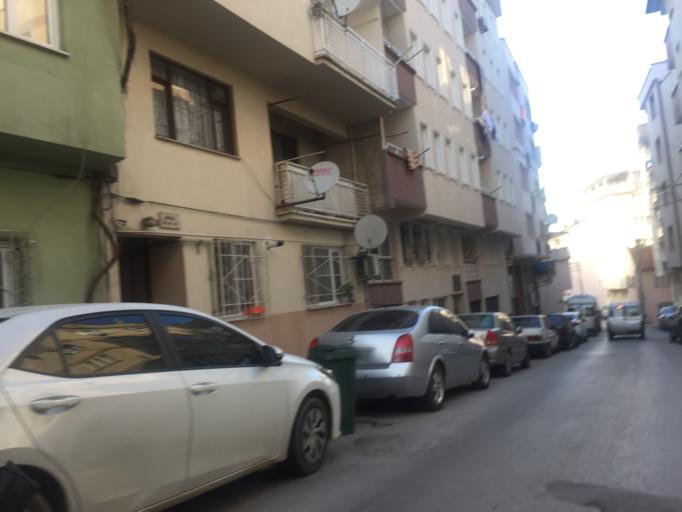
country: TR
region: Bursa
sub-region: Osmangazi
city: Bursa
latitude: 40.1873
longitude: 29.0838
